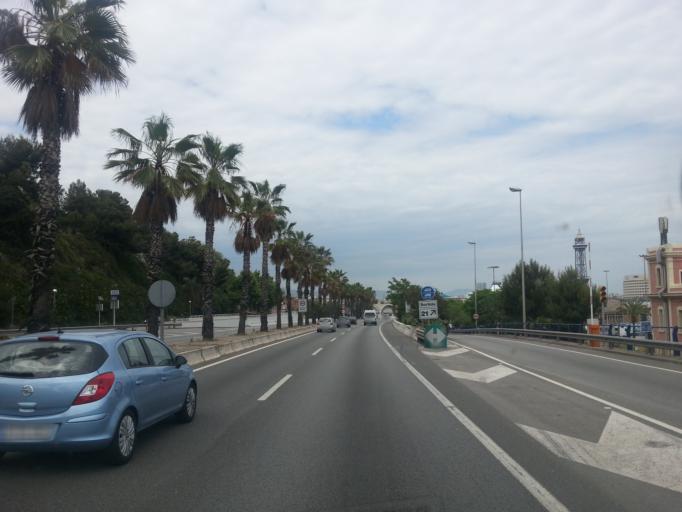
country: ES
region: Catalonia
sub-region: Provincia de Barcelona
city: Ciutat Vella
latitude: 41.3668
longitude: 2.1724
